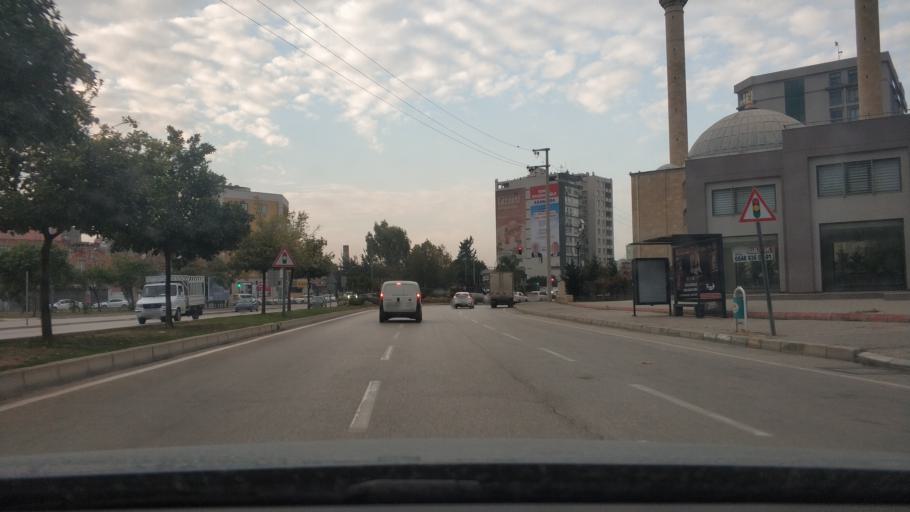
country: TR
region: Adana
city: Adana
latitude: 36.9941
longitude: 35.3190
